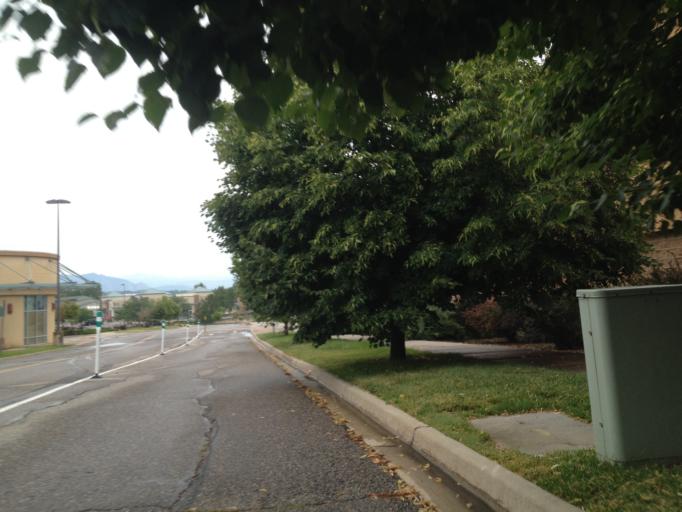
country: US
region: Colorado
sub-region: Broomfield County
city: Broomfield
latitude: 39.9301
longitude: -105.1210
